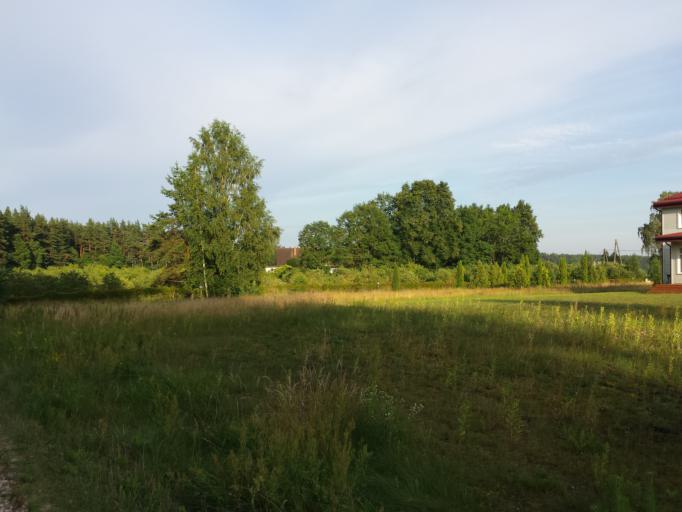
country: LV
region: Kekava
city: Kekava
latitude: 56.8635
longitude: 24.2116
